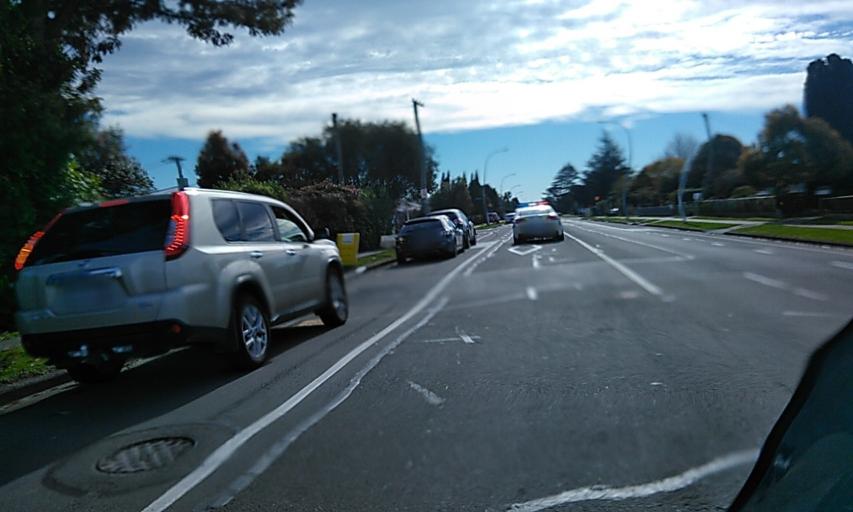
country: NZ
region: Gisborne
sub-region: Gisborne District
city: Gisborne
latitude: -38.6422
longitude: 178.0081
